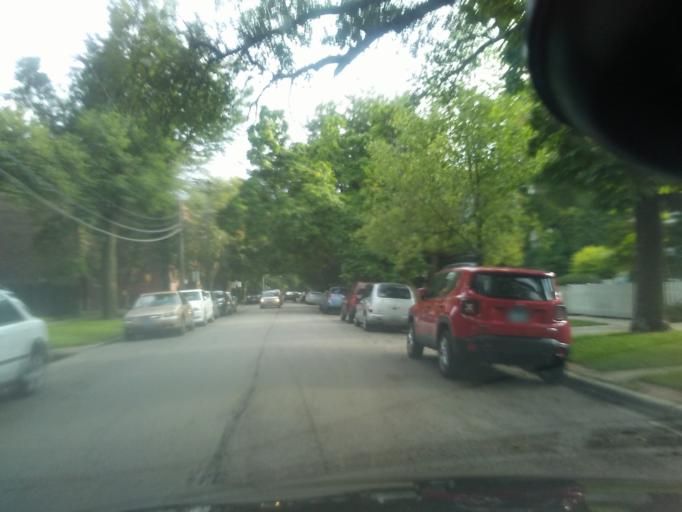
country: US
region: Illinois
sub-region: Cook County
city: Evanston
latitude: 42.0049
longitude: -87.6657
